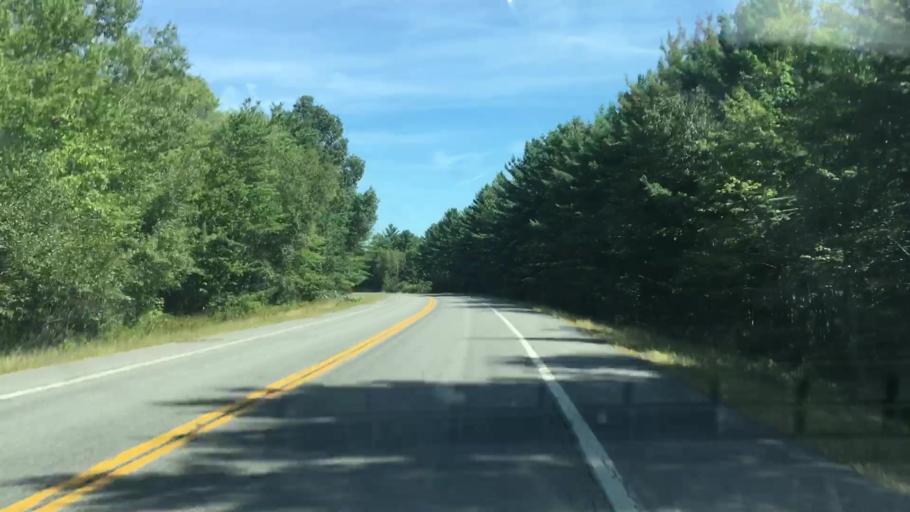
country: US
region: Maine
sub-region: Piscataquis County
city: Milo
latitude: 45.2290
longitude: -68.9484
